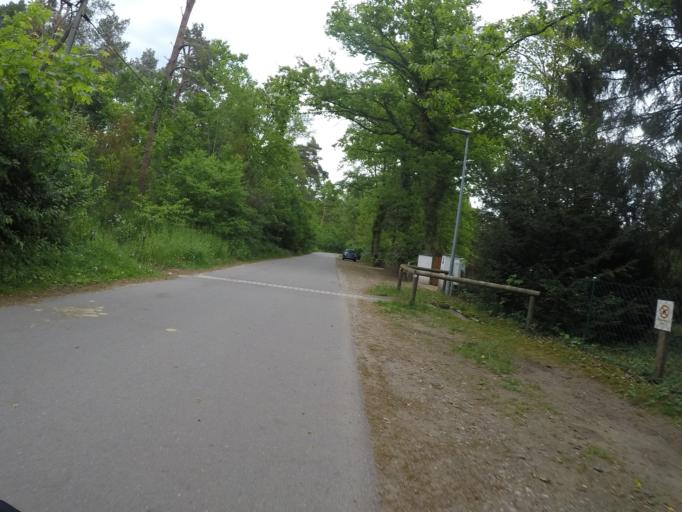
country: DE
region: Schleswig-Holstein
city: Norderstedt
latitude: 53.7098
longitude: 9.9701
